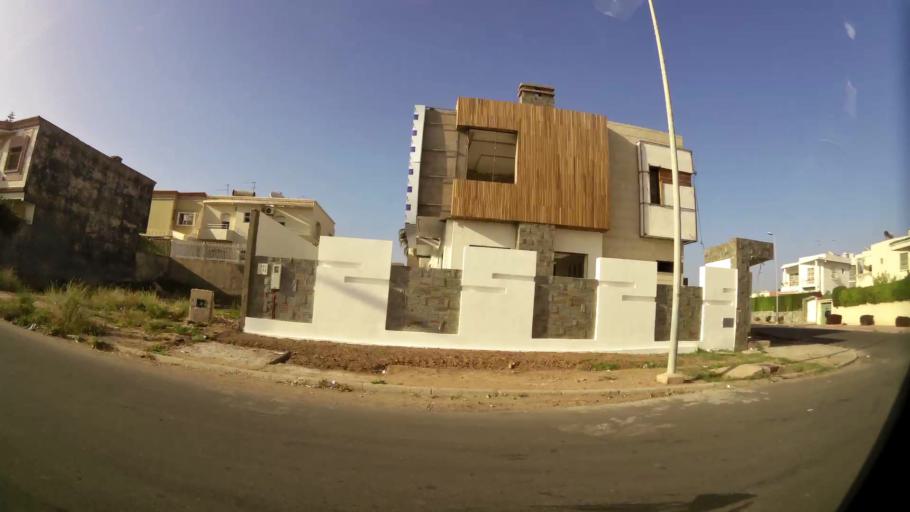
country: MA
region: Oued ed Dahab-Lagouira
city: Dakhla
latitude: 30.4009
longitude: -9.5395
